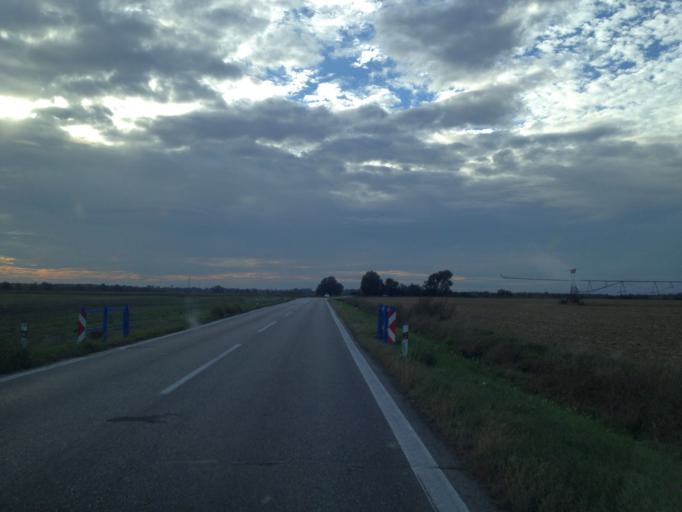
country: SK
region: Nitriansky
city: Komarno
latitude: 47.7606
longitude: 18.1922
